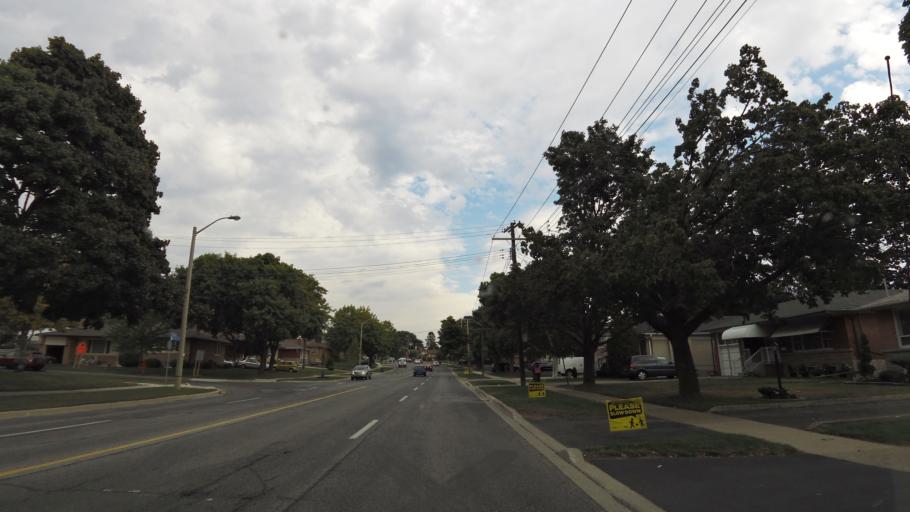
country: CA
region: Ontario
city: Etobicoke
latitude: 43.6902
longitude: -79.5382
